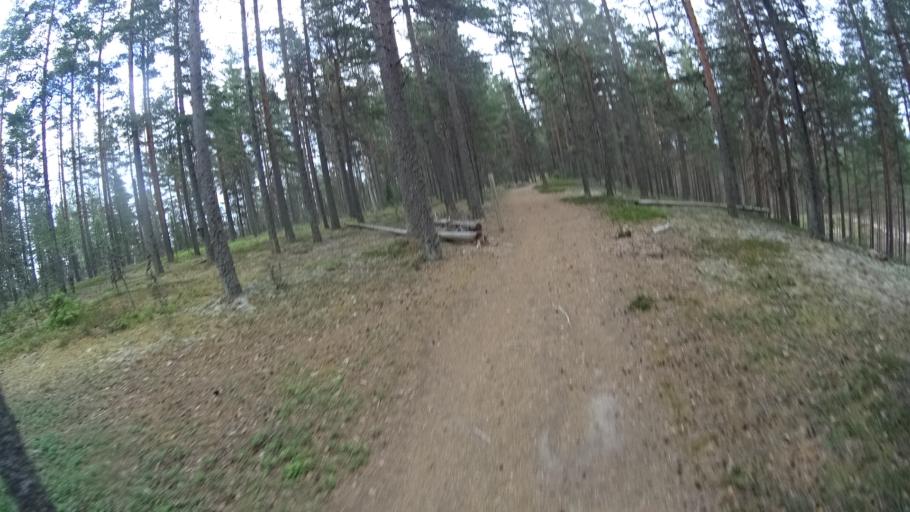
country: FI
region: Satakunta
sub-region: Pohjois-Satakunta
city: Jaemijaervi
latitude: 61.7739
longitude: 22.7288
